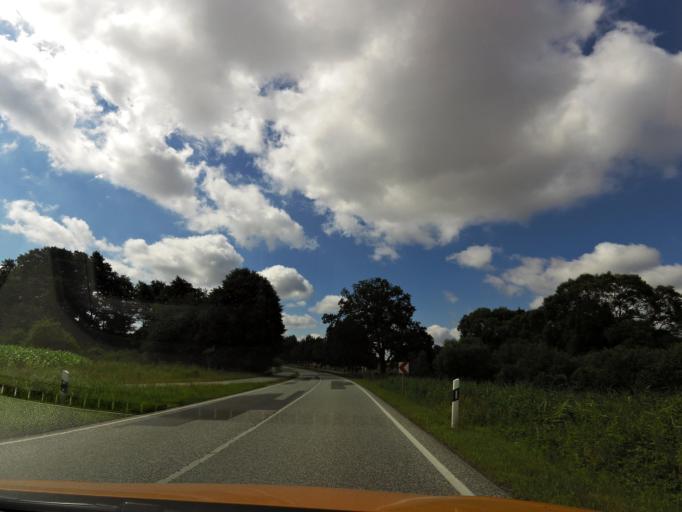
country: DE
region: Mecklenburg-Vorpommern
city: Plau am See
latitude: 53.5078
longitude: 12.2673
